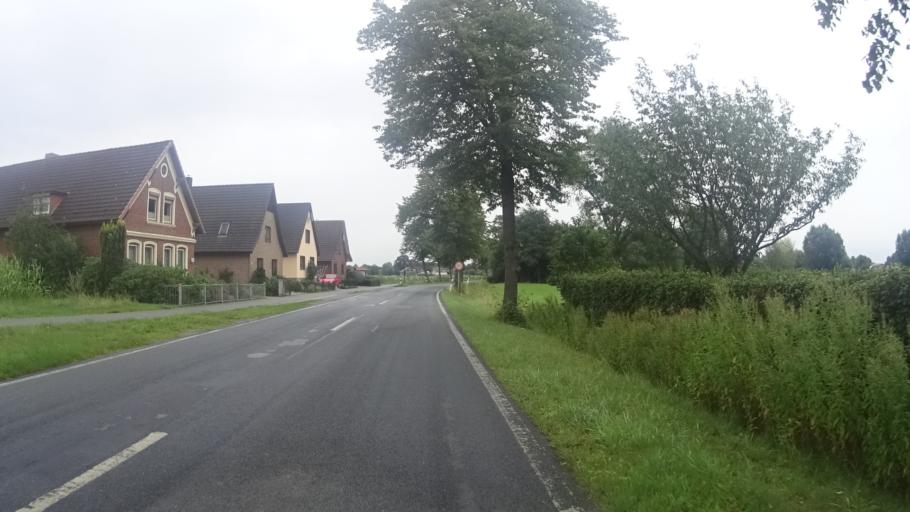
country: DE
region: Schleswig-Holstein
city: Bevern
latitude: 53.7570
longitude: 9.7610
